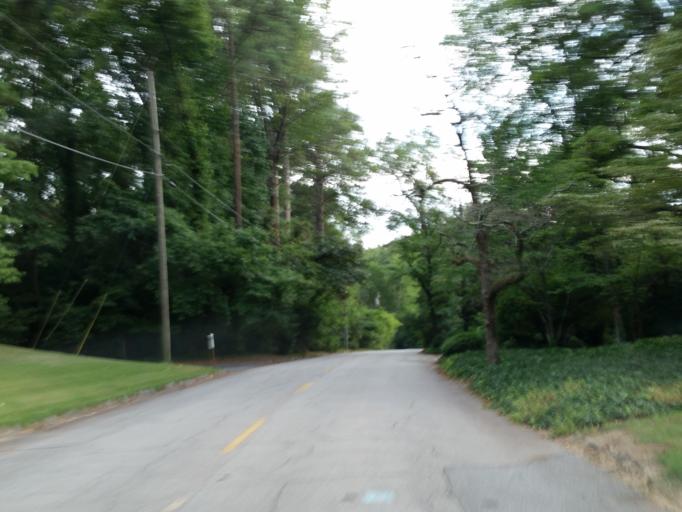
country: US
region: Georgia
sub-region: Cobb County
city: Vinings
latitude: 33.8470
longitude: -84.4415
